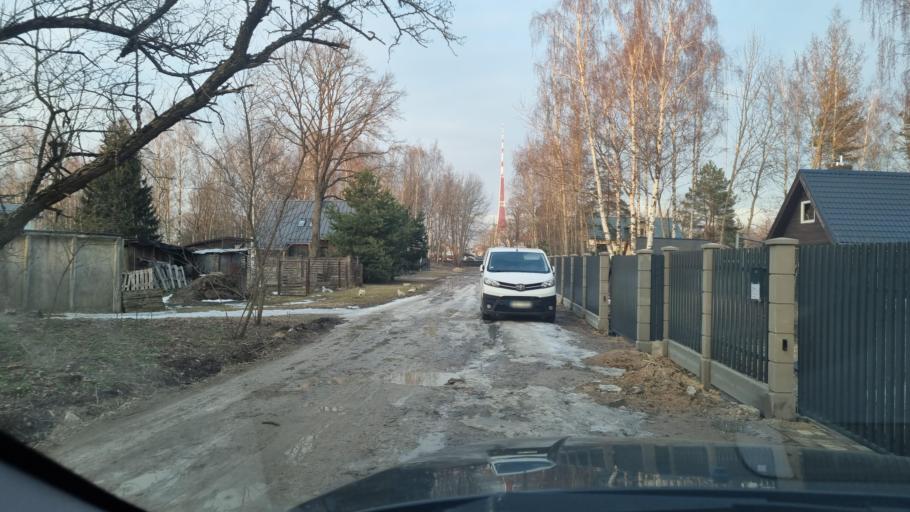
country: LV
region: Kekava
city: Balozi
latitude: 56.9105
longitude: 24.1208
